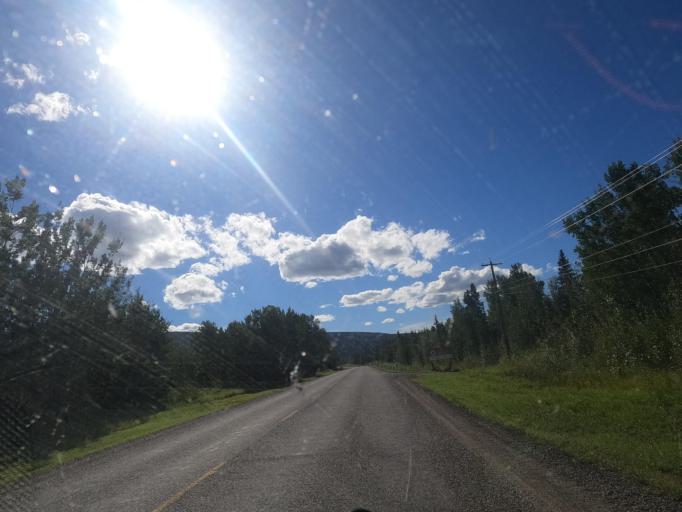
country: CA
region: Yukon
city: Dawson City
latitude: 64.0366
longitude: -139.1516
